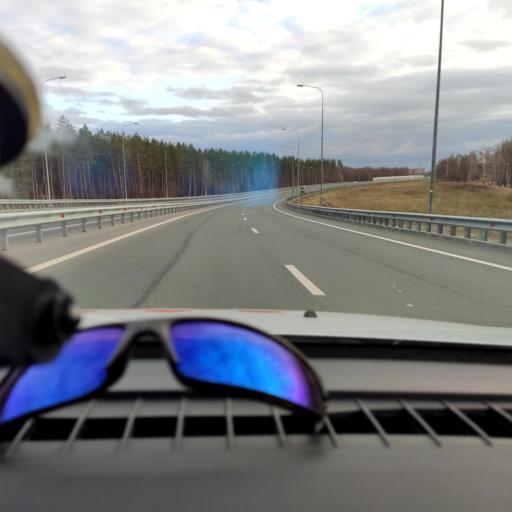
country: RU
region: Samara
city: Bereza
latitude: 53.5041
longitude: 50.1198
